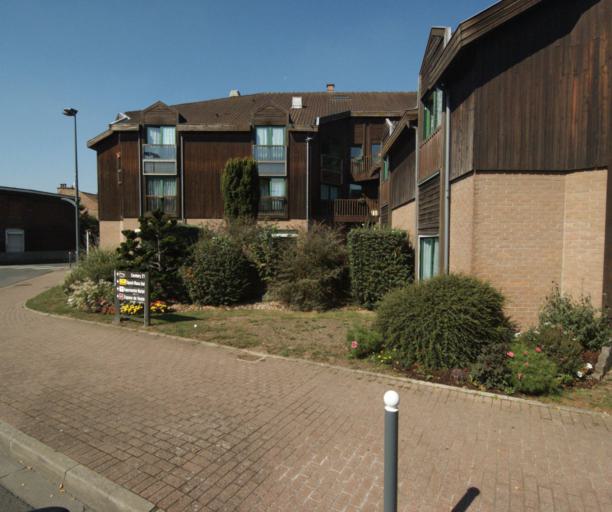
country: FR
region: Nord-Pas-de-Calais
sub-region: Departement du Nord
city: Mons-en-Baroeul
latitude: 50.6340
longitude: 3.1143
